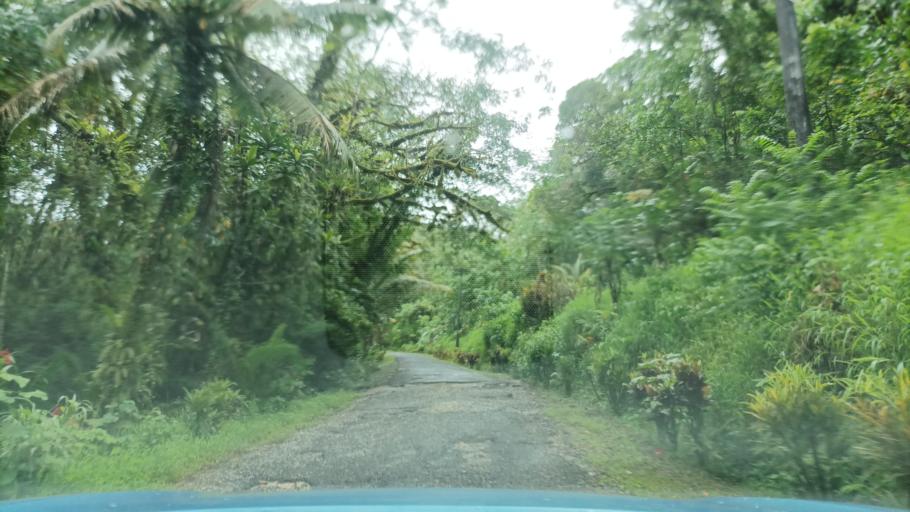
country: FM
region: Pohnpei
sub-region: Sokehs Municipality
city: Palikir - National Government Center
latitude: 6.8272
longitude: 158.1699
